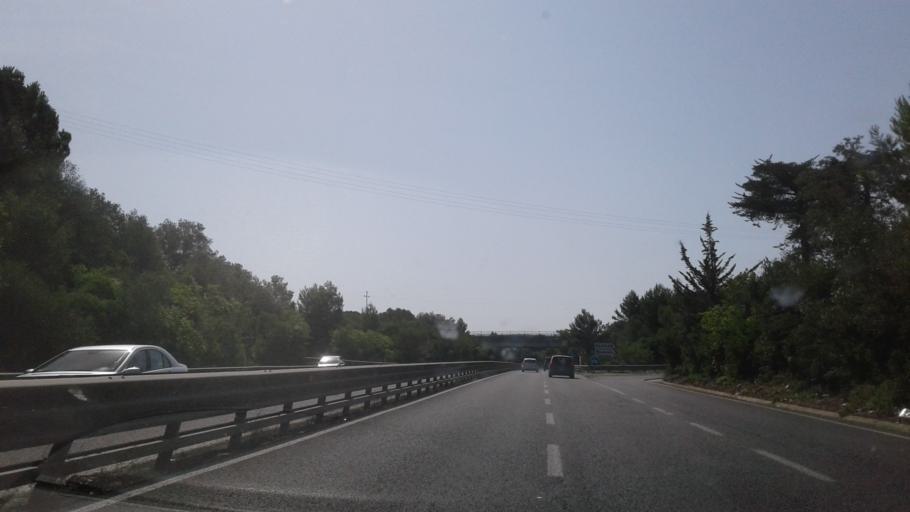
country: IT
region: Sardinia
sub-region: Provincia di Sassari
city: Sassari
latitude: 40.7061
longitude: 8.5505
